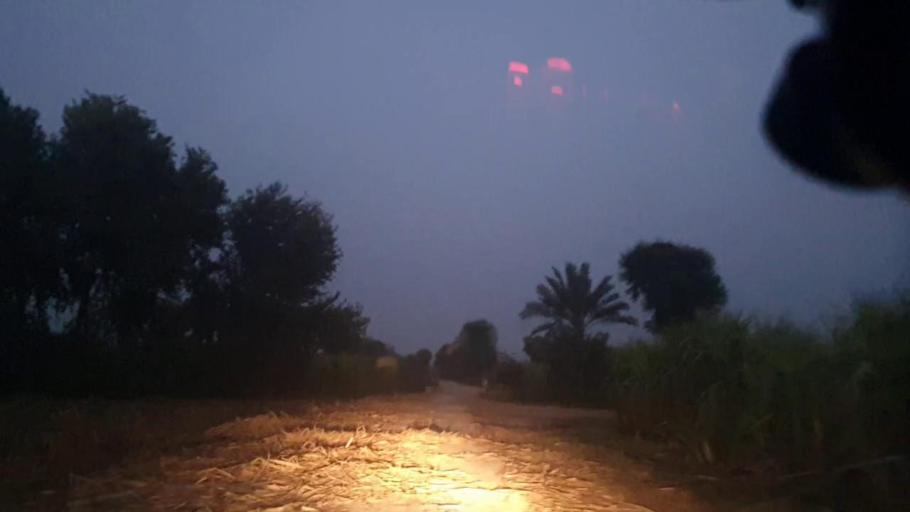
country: PK
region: Sindh
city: Hingorja
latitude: 27.2125
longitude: 68.3739
